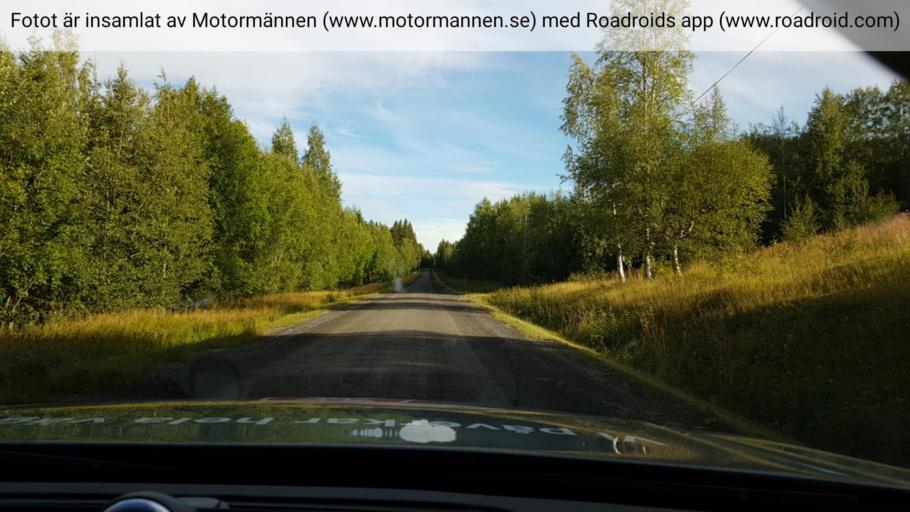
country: SE
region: Jaemtland
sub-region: Stroemsunds Kommun
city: Stroemsund
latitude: 64.1070
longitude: 15.8184
